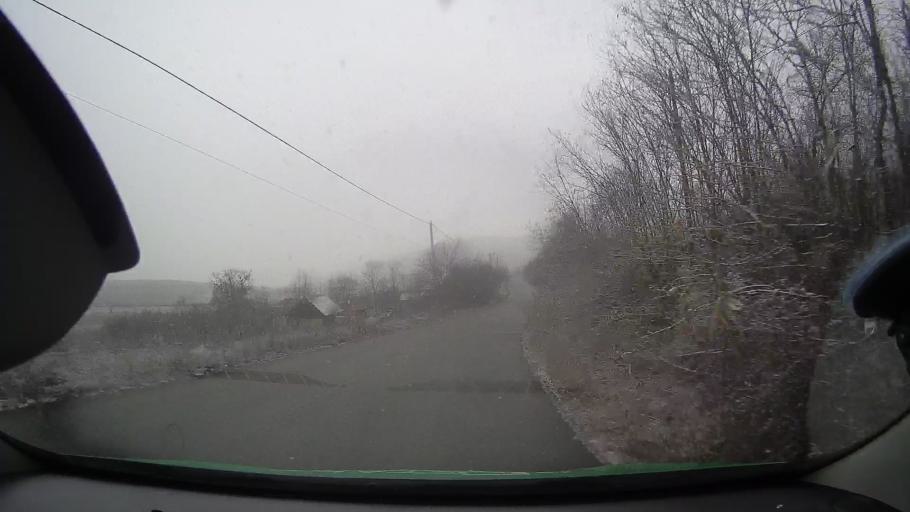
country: RO
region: Alba
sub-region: Comuna Noslac
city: Noslac
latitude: 46.3571
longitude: 23.9311
